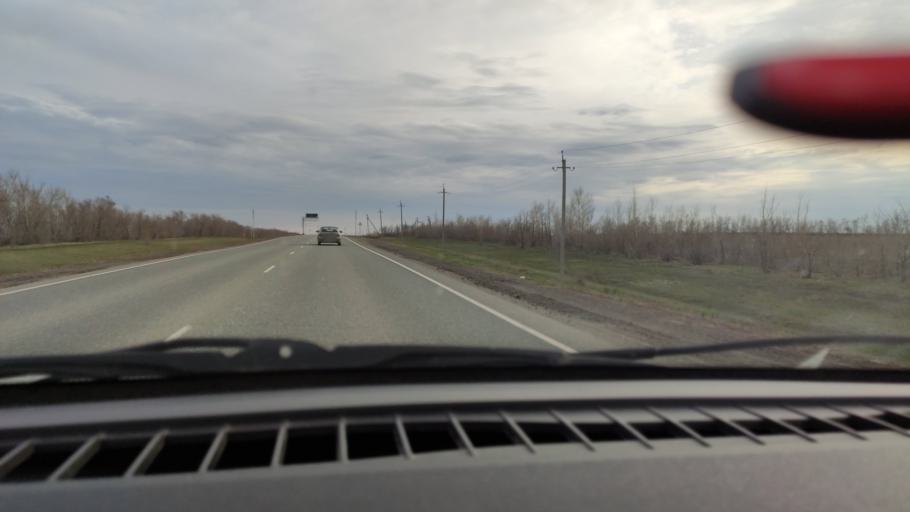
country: RU
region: Orenburg
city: Tatarskaya Kargala
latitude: 52.0021
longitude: 55.1986
